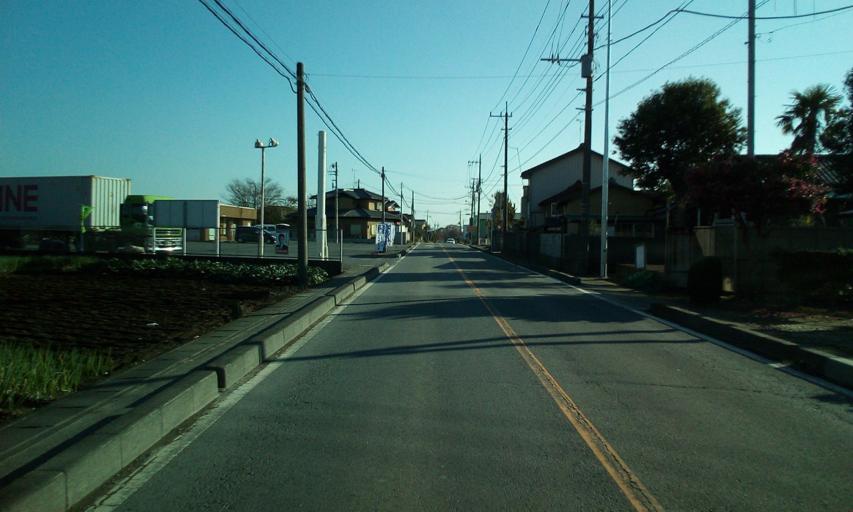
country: JP
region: Chiba
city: Noda
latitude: 35.9480
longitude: 139.8370
